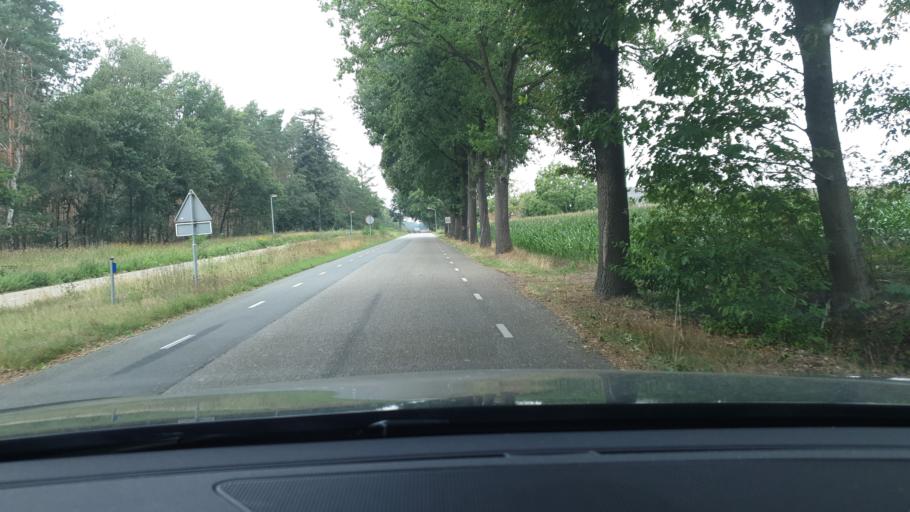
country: NL
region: North Brabant
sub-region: Gemeente Oirschot
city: Oostelbeers
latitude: 51.4486
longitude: 5.3004
